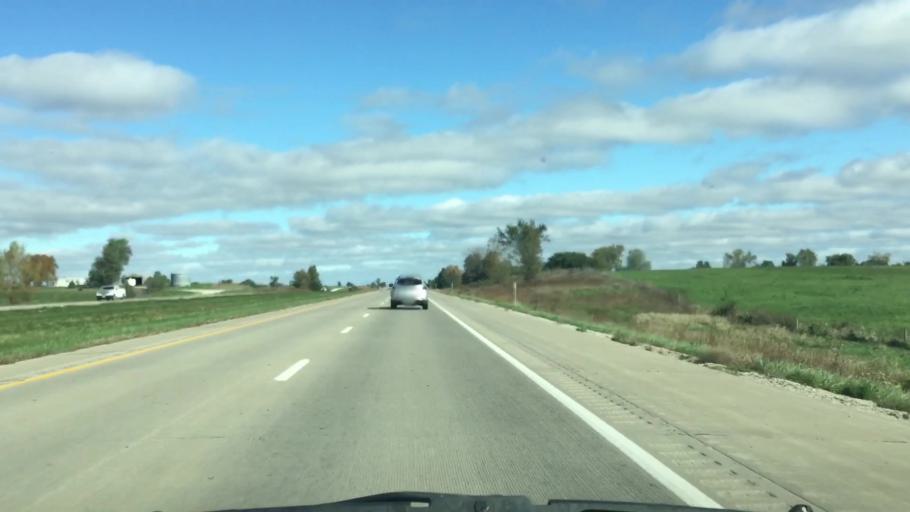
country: US
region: Iowa
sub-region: Decatur County
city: Leon
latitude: 40.7647
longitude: -93.8363
